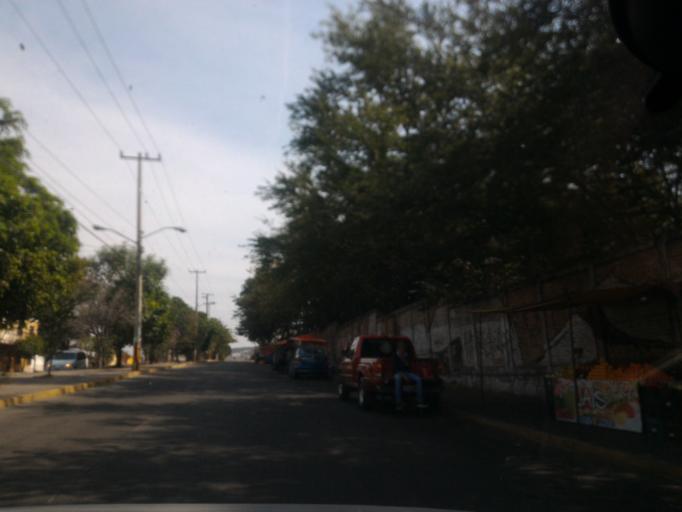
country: MX
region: Jalisco
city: Guadalajara
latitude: 20.6181
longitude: -103.3854
